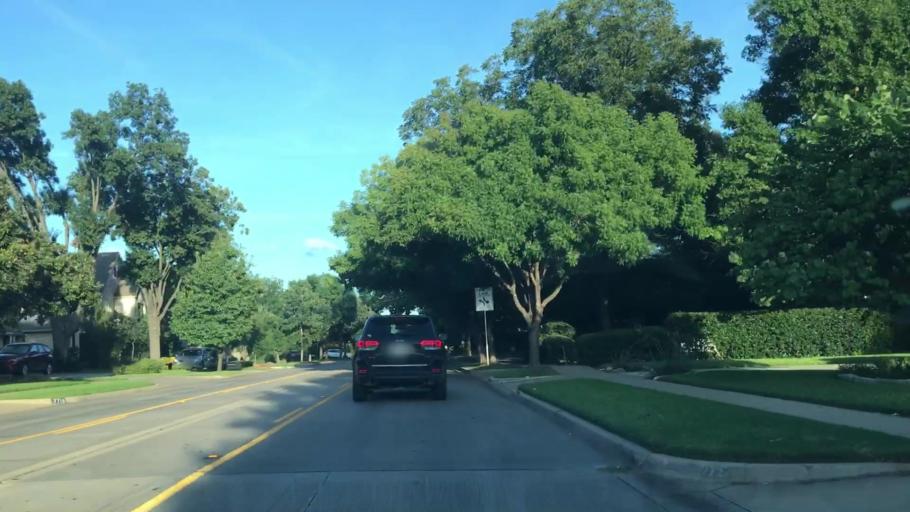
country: US
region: Texas
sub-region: Dallas County
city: Highland Park
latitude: 32.8511
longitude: -96.7750
